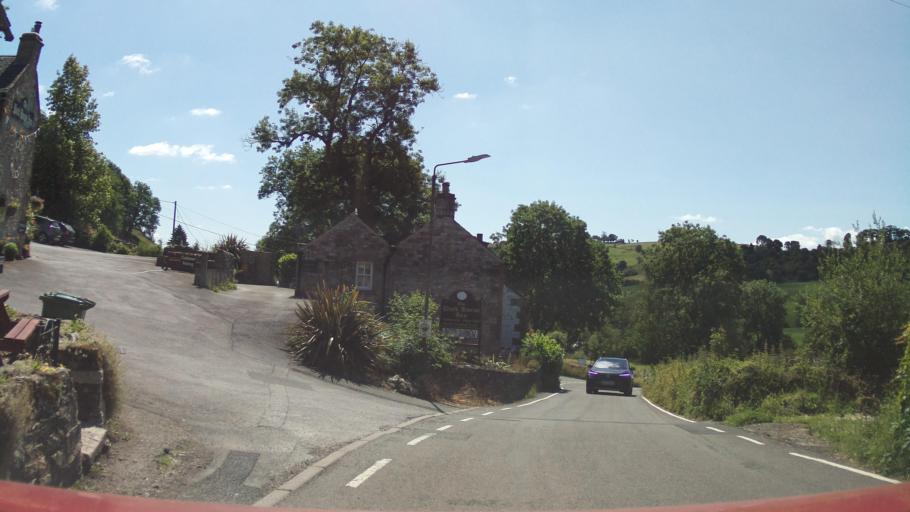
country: GB
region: England
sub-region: Derbyshire
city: Buxton
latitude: 53.1838
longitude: -1.8507
